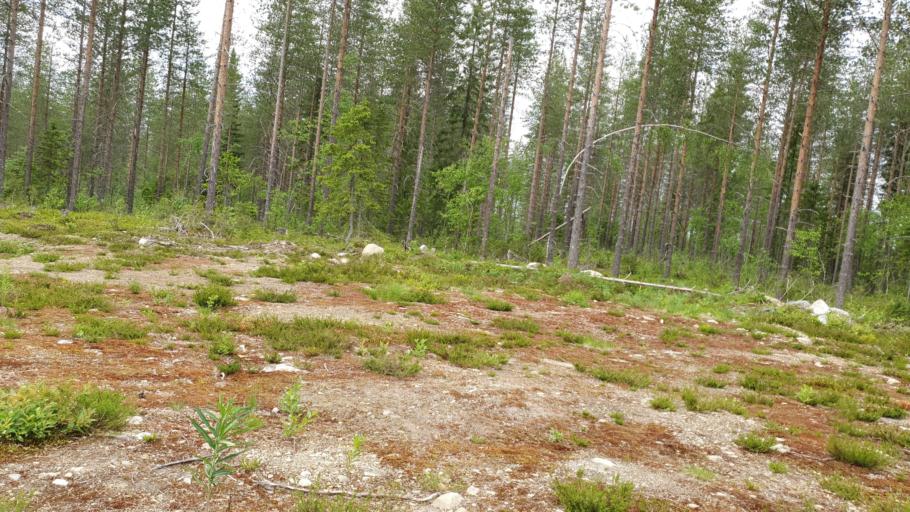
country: FI
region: Kainuu
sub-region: Kehys-Kainuu
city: Kuhmo
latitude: 64.4466
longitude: 29.6849
